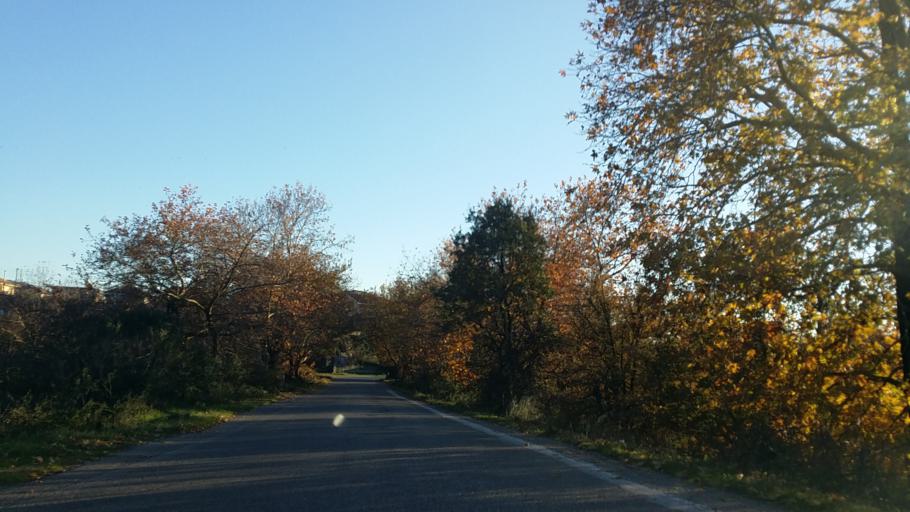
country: GR
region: West Greece
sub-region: Nomos Aitolias kai Akarnanias
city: Lepenou
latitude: 38.7404
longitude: 21.3458
